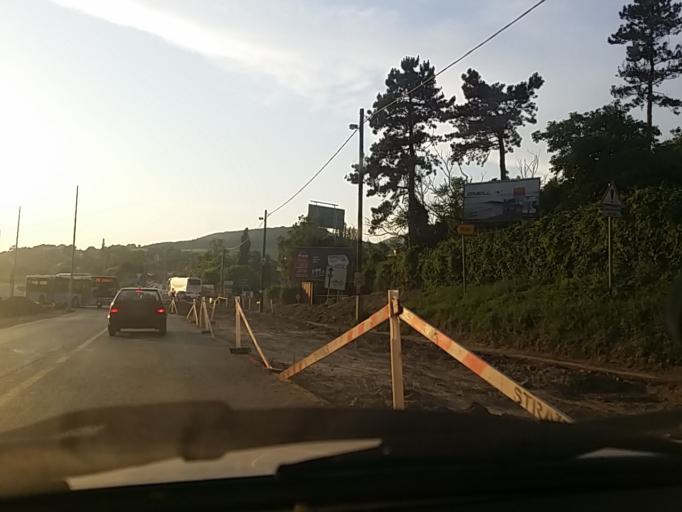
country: HU
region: Pest
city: Urom
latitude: 47.5828
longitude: 19.0004
